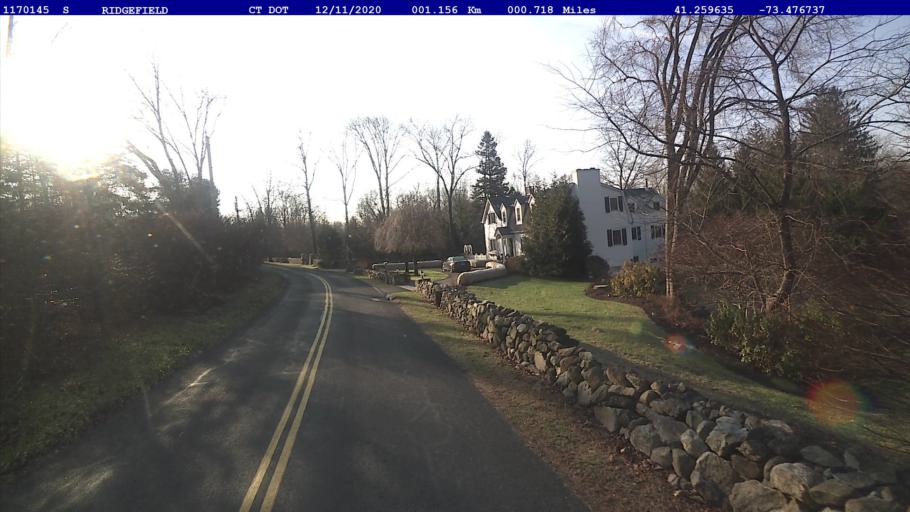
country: US
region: Connecticut
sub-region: Fairfield County
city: Ridgefield
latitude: 41.2596
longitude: -73.4767
